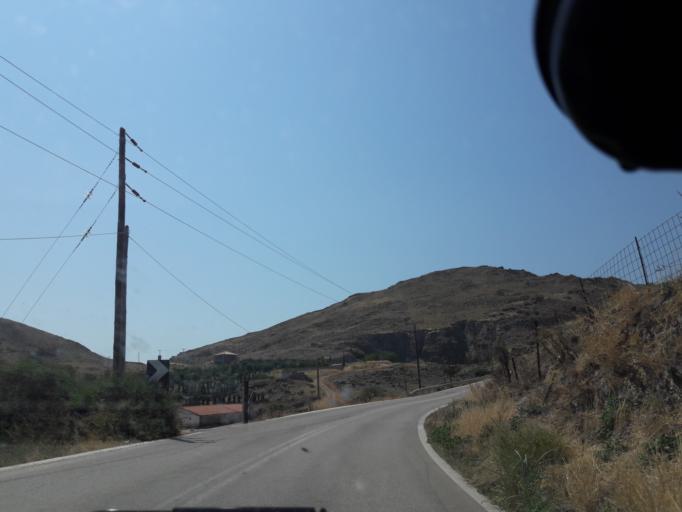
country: GR
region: North Aegean
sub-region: Nomos Lesvou
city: Myrina
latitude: 39.8516
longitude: 25.0992
